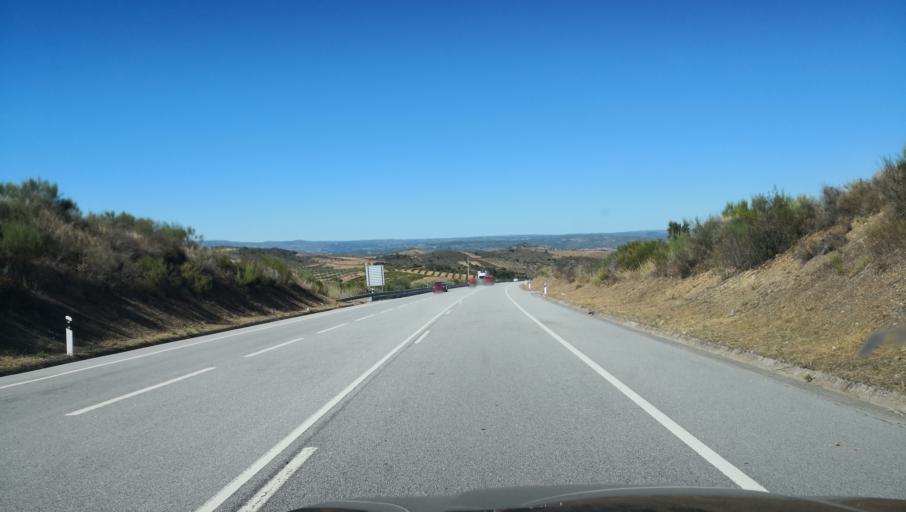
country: PT
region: Braganca
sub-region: Mirandela
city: Mirandela
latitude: 41.4926
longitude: -7.2270
